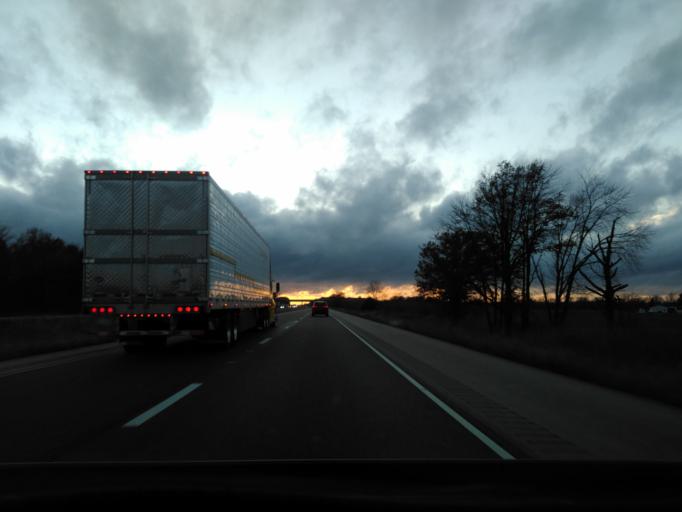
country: US
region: Illinois
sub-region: Effingham County
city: Altamont
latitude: 39.0404
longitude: -88.7618
